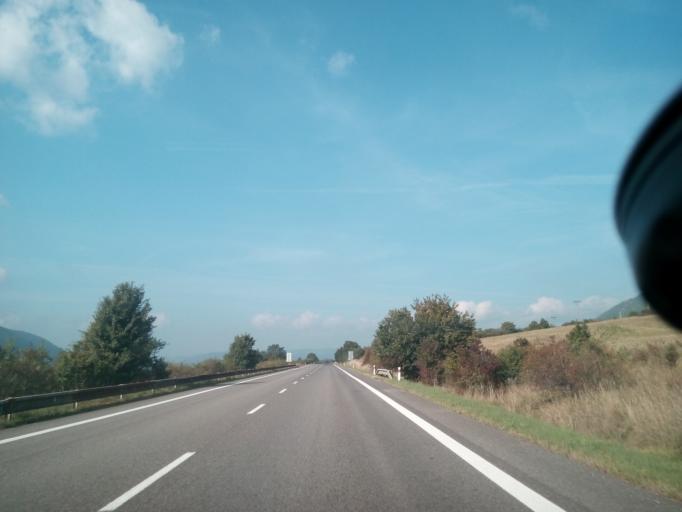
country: SK
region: Kosicky
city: Roznava
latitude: 48.5963
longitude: 20.7073
